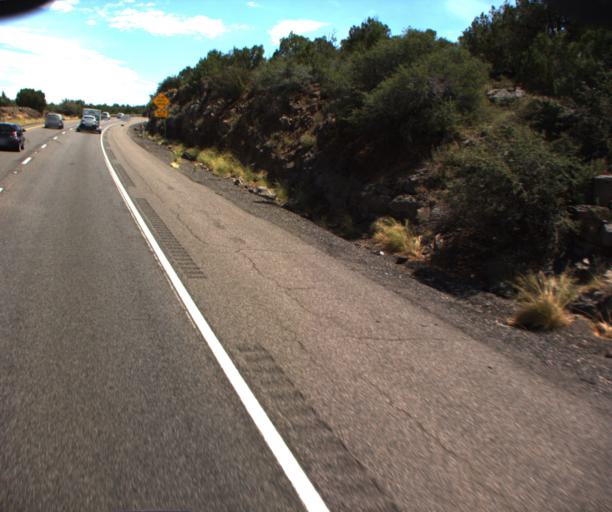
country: US
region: Arizona
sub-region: Yavapai County
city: Village of Oak Creek (Big Park)
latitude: 34.7715
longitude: -111.6384
